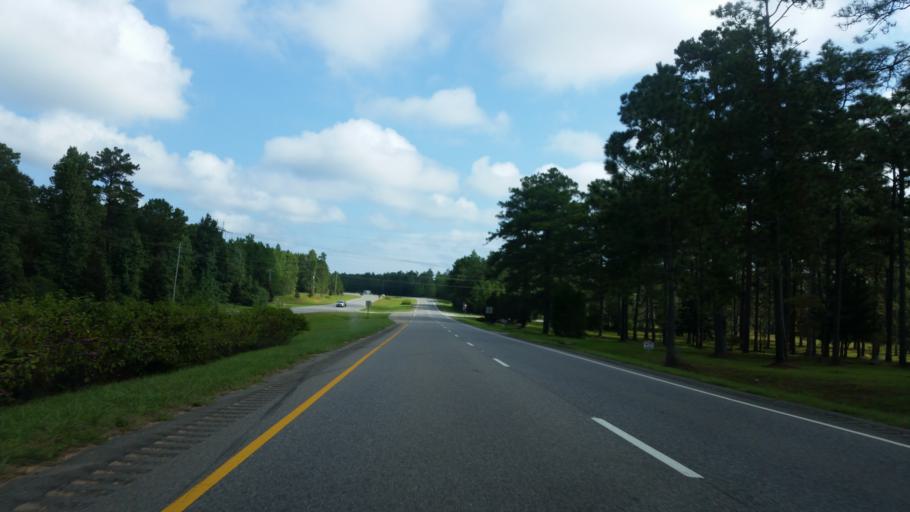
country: US
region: Alabama
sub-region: Baldwin County
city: Bay Minette
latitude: 30.9237
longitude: -87.7722
